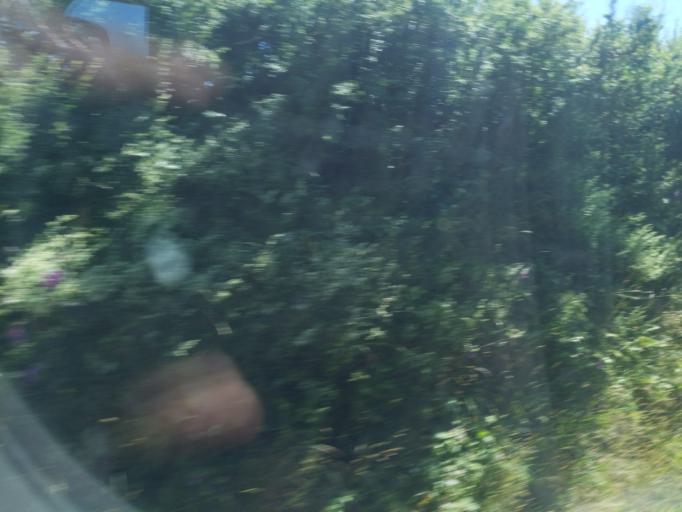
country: GB
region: England
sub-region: Cornwall
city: Saint Stephen
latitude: 50.3323
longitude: -4.8488
